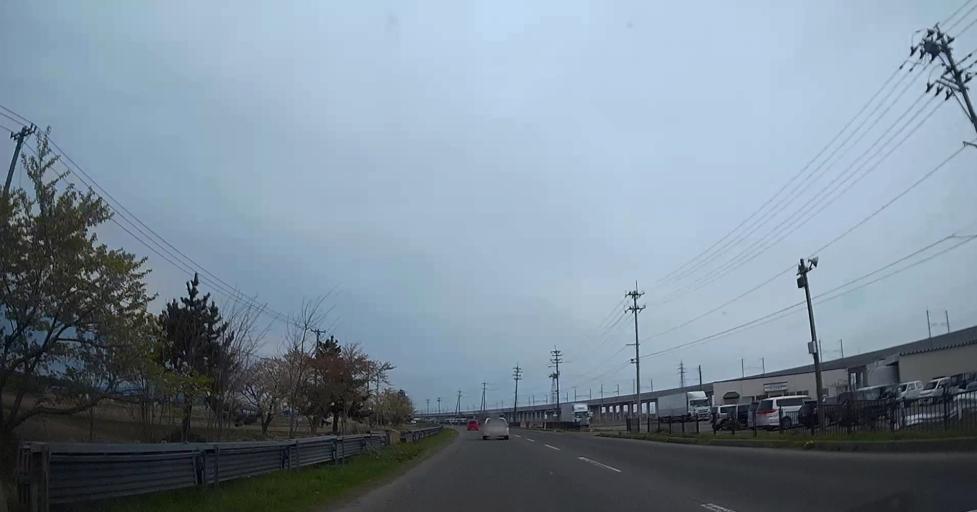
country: JP
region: Aomori
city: Aomori Shi
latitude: 40.8391
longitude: 140.6907
